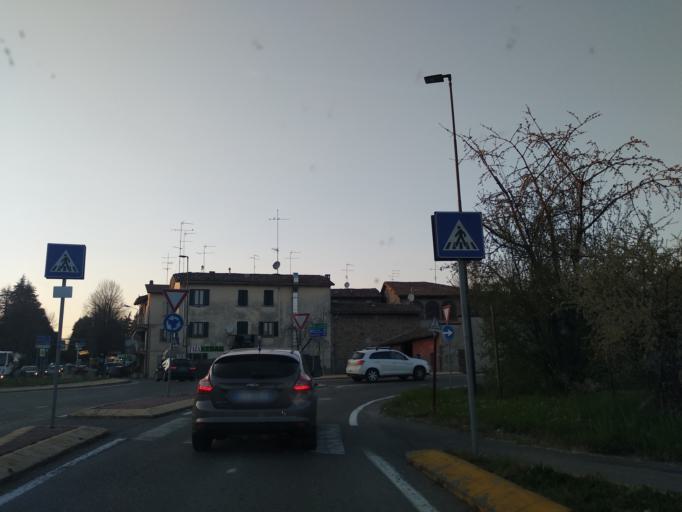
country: IT
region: Emilia-Romagna
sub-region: Provincia di Reggio Emilia
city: Puianello
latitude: 44.6258
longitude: 10.5647
